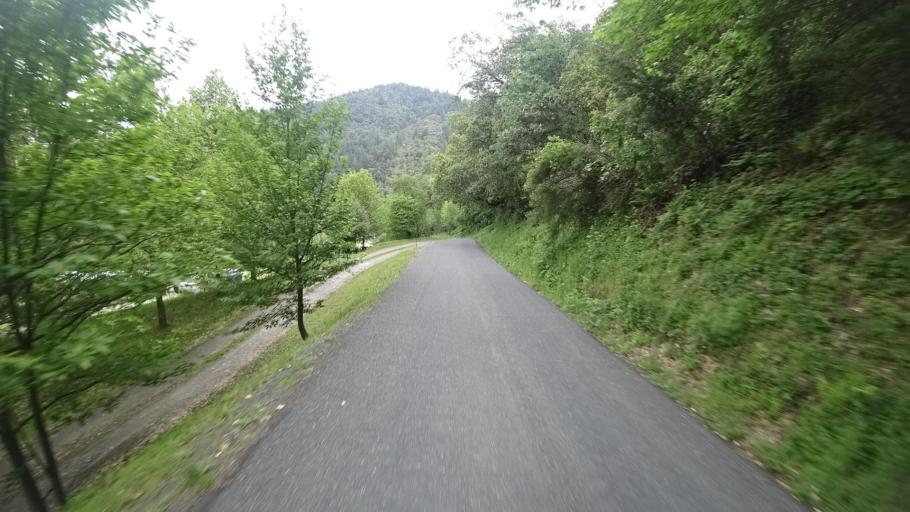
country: US
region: California
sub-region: Humboldt County
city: Willow Creek
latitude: 40.9435
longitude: -123.6116
